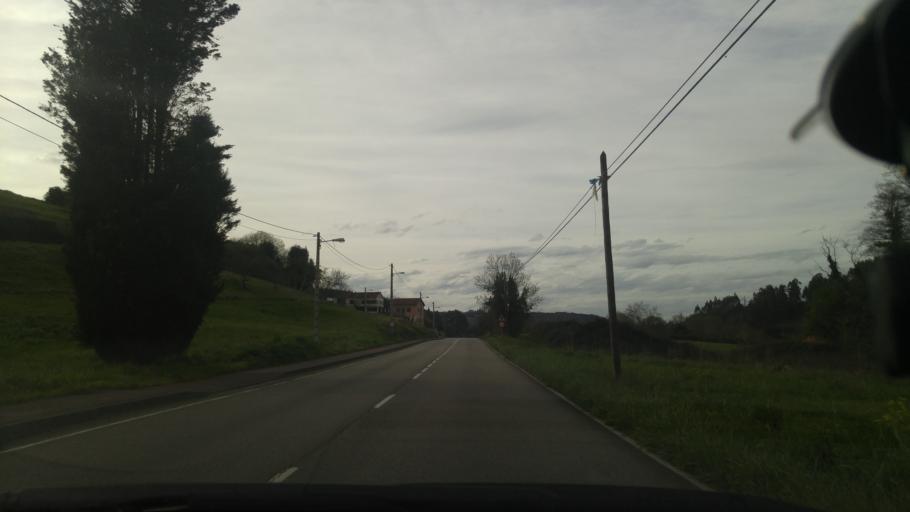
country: ES
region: Asturias
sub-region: Province of Asturias
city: Corvera de Asturias
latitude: 43.4950
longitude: -5.8541
